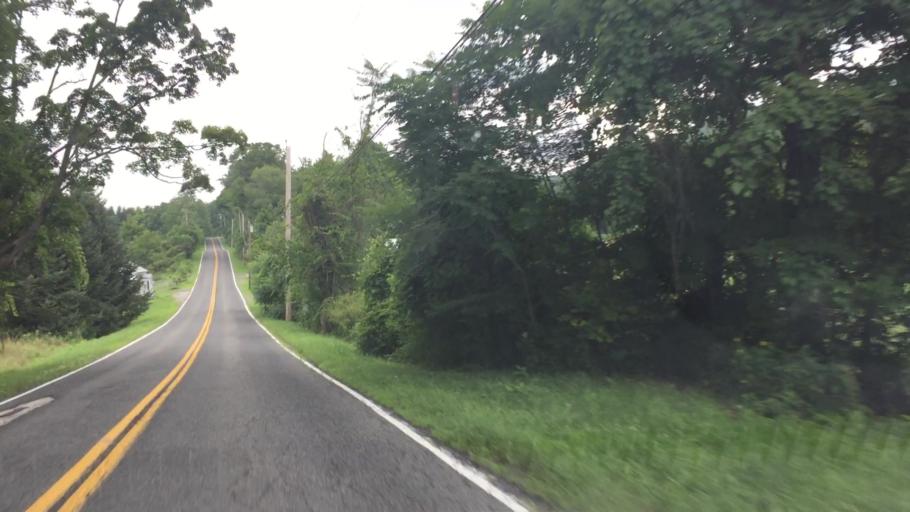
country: US
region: Massachusetts
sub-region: Berkshire County
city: Housatonic
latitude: 42.2999
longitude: -73.4028
